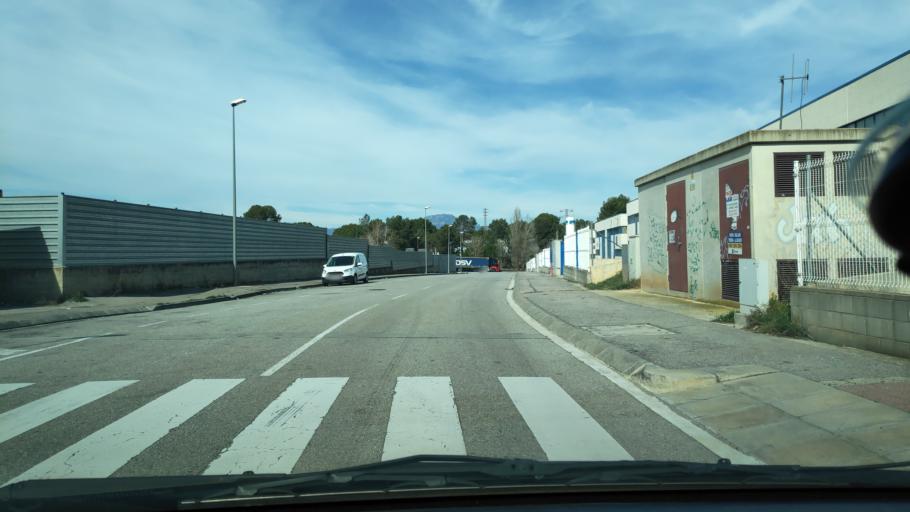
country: ES
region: Catalonia
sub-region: Provincia de Barcelona
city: Rubi
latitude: 41.5110
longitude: 2.0382
